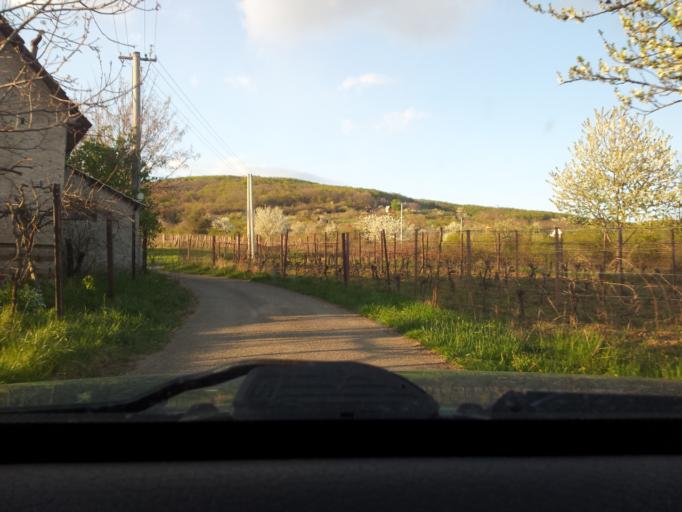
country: SK
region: Nitriansky
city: Tlmace
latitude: 48.3017
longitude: 18.5610
